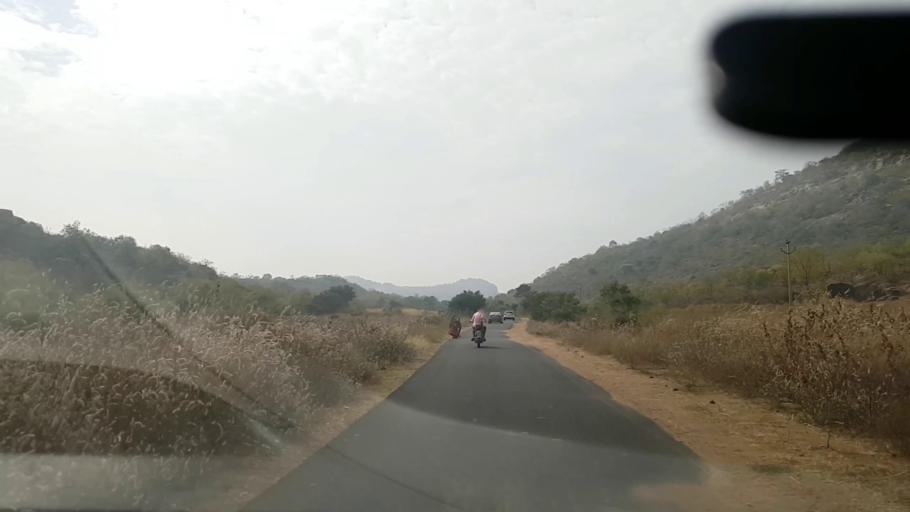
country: IN
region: Telangana
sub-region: Rangareddi
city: Ghatkesar
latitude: 17.1879
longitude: 78.8245
